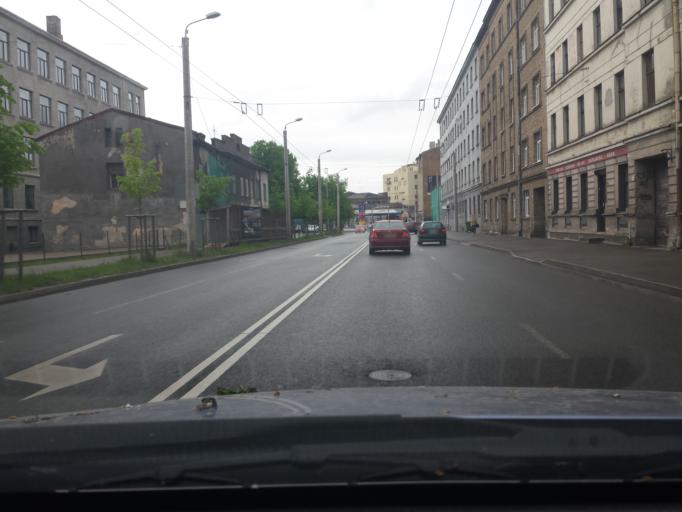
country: LV
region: Riga
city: Riga
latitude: 56.9621
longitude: 24.1513
